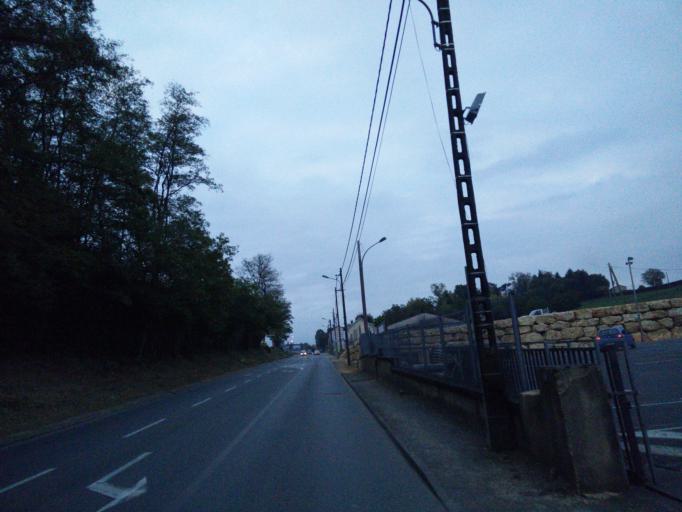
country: FR
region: Aquitaine
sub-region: Departement de la Dordogne
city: Sarlat-la-Caneda
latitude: 44.8764
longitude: 1.2199
